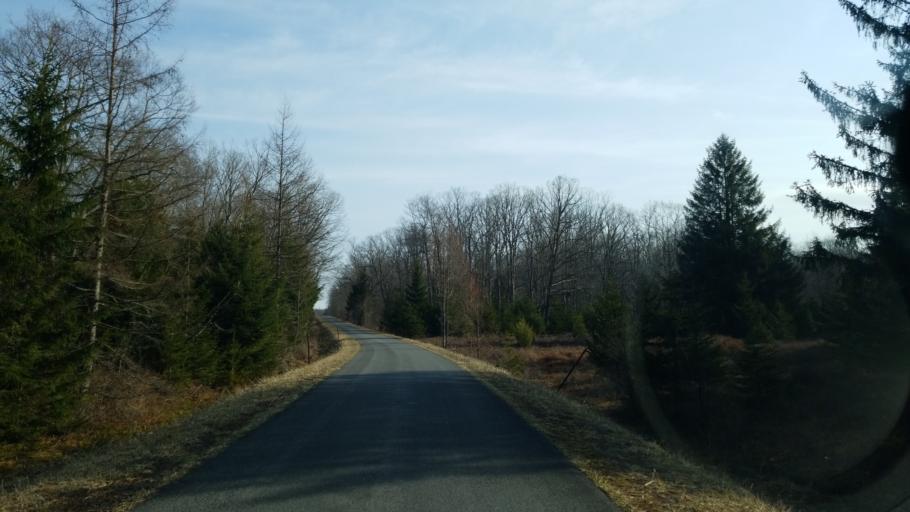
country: US
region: Pennsylvania
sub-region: Clearfield County
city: Shiloh
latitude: 41.2298
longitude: -78.2117
